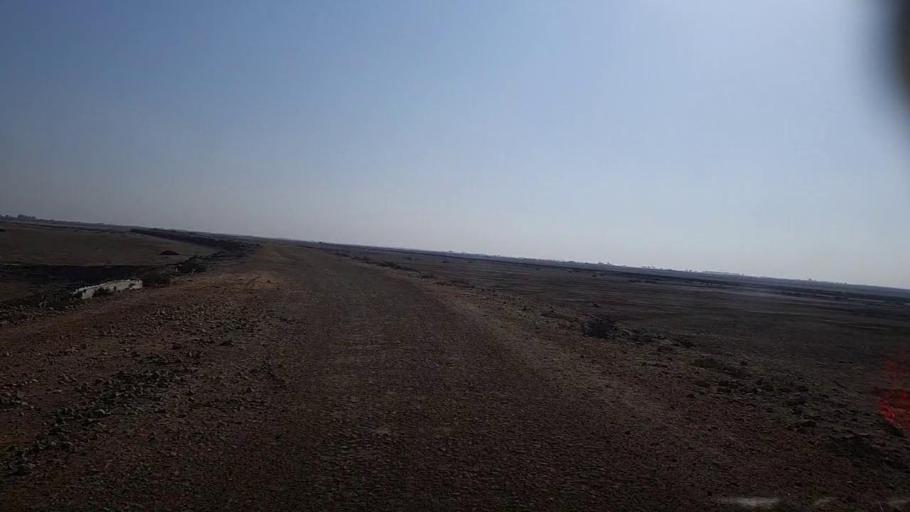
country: PK
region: Sindh
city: Mirpur Sakro
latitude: 24.5170
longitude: 67.4943
